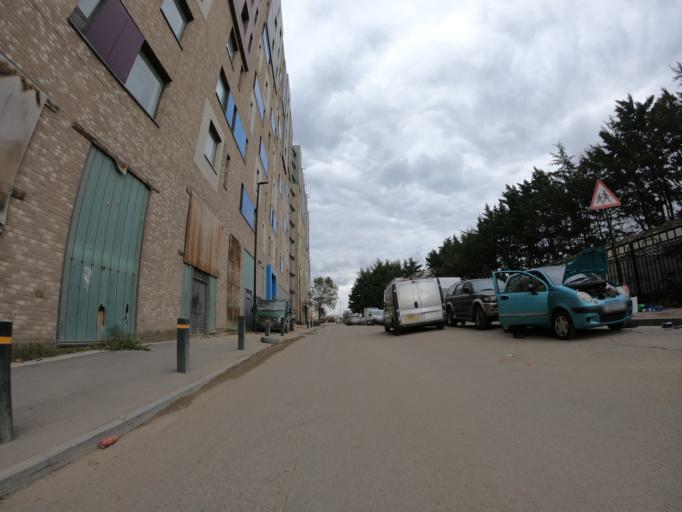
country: GB
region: England
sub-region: Greater London
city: Blackheath
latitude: 51.4920
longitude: 0.0191
